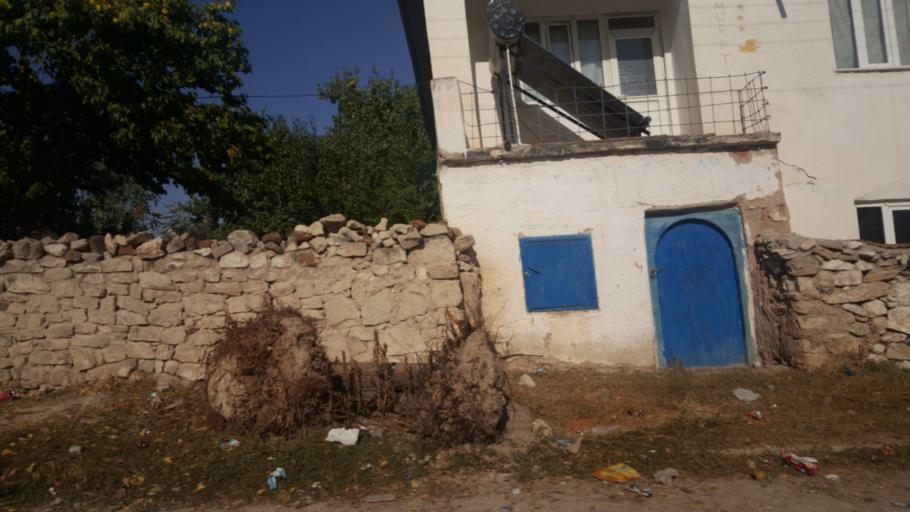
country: TR
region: Konya
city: Celtik
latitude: 39.0590
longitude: 31.8377
